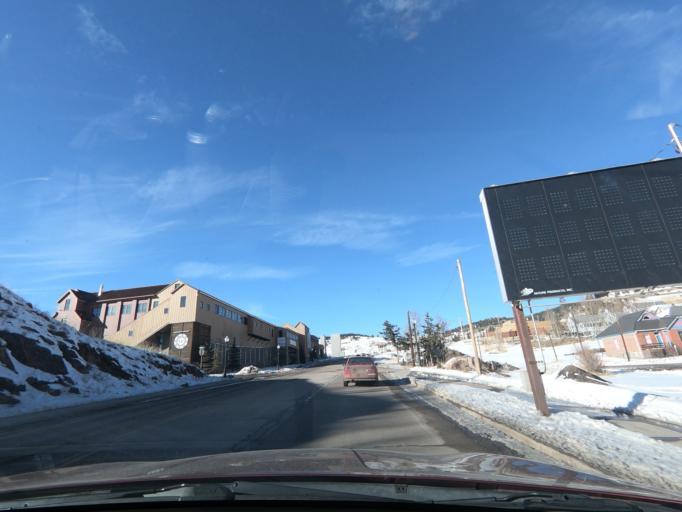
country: US
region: Colorado
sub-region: Teller County
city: Cripple Creek
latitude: 38.7492
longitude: -105.1729
